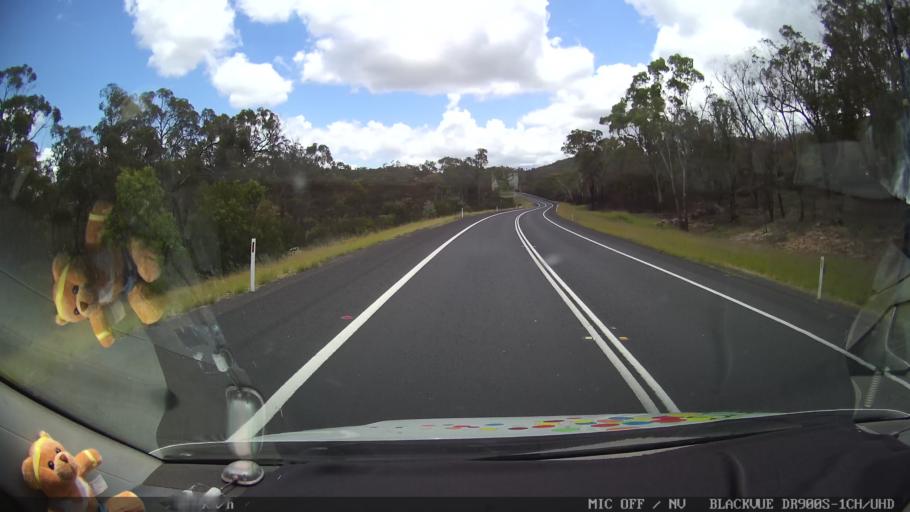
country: AU
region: New South Wales
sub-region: Glen Innes Severn
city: Glen Innes
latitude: -29.3558
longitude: 151.8972
